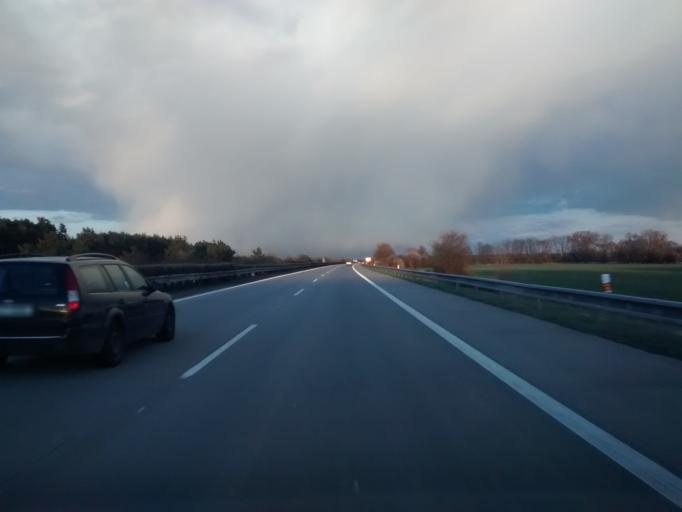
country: CZ
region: Central Bohemia
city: Pecky
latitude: 50.1237
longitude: 15.0302
